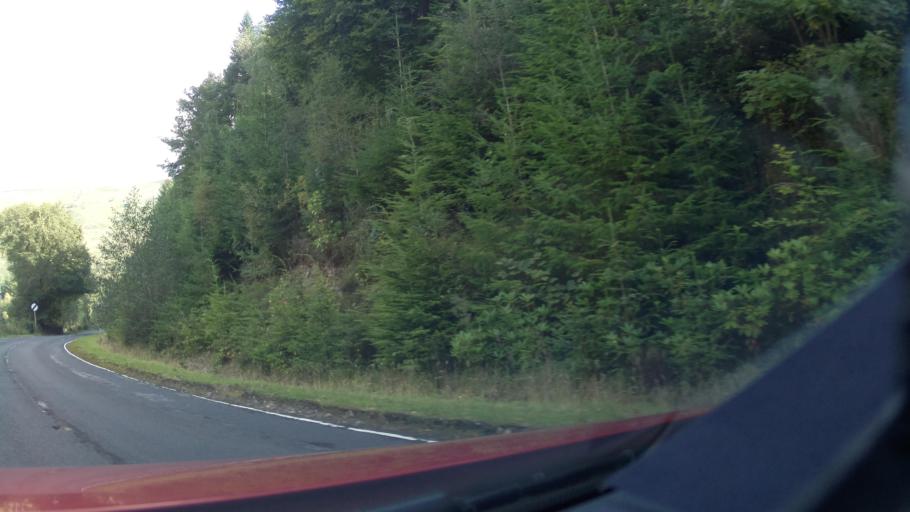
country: GB
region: Scotland
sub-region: Highland
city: Spean Bridge
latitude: 57.0672
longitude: -4.7890
